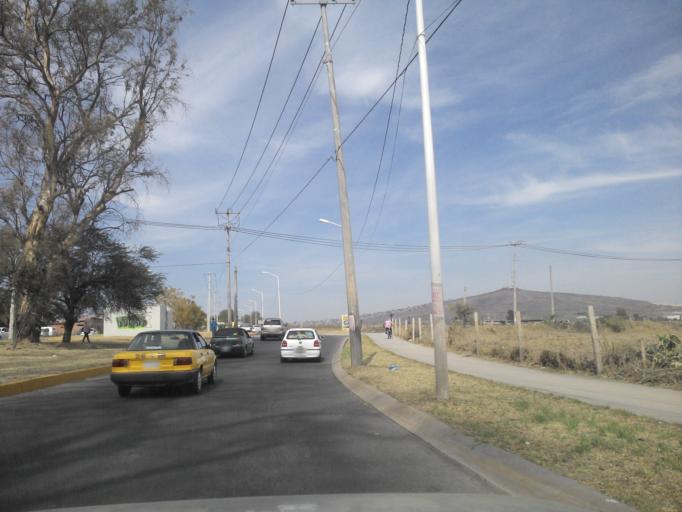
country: MX
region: Jalisco
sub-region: San Pedro Tlaquepaque
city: Paseo del Prado
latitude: 20.5665
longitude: -103.3918
